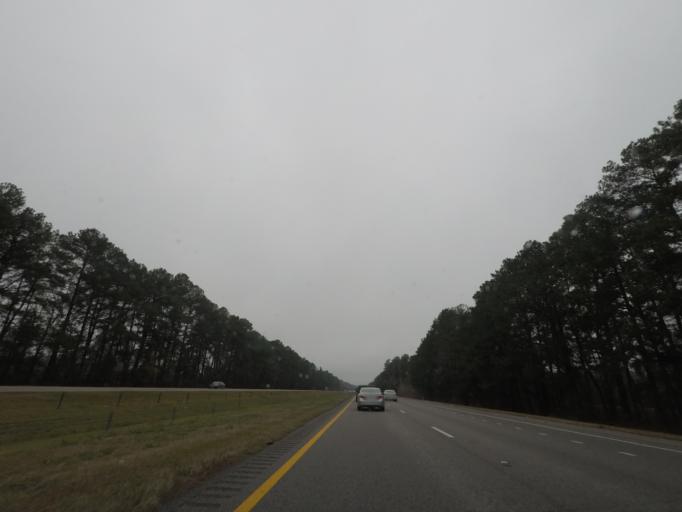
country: US
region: South Carolina
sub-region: Florence County
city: Timmonsville
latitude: 33.9434
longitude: -80.0605
